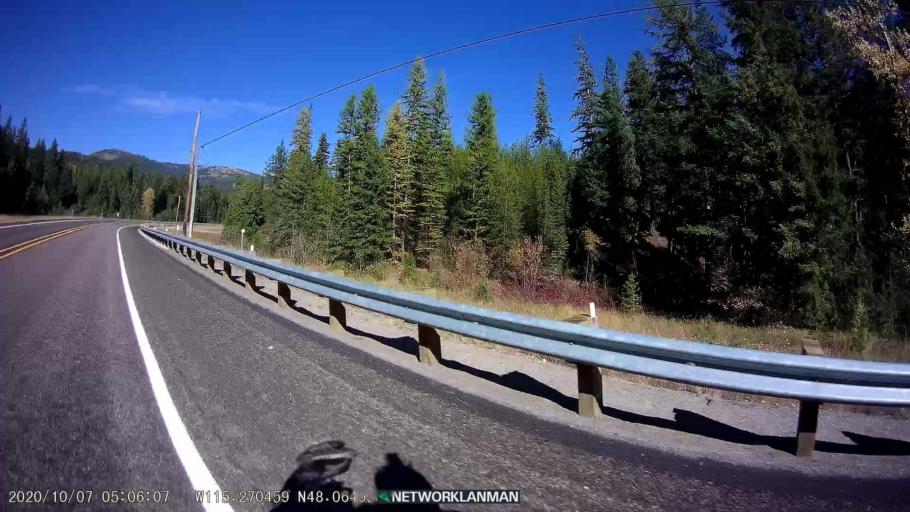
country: US
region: Montana
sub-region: Lincoln County
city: Libby
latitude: 48.0650
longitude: -115.2709
